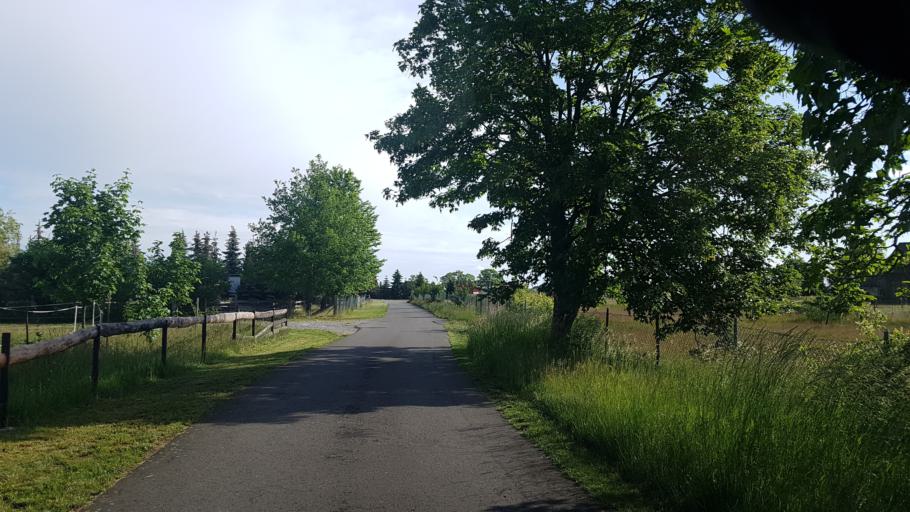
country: DE
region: Brandenburg
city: Crinitz
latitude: 51.8078
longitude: 13.8216
